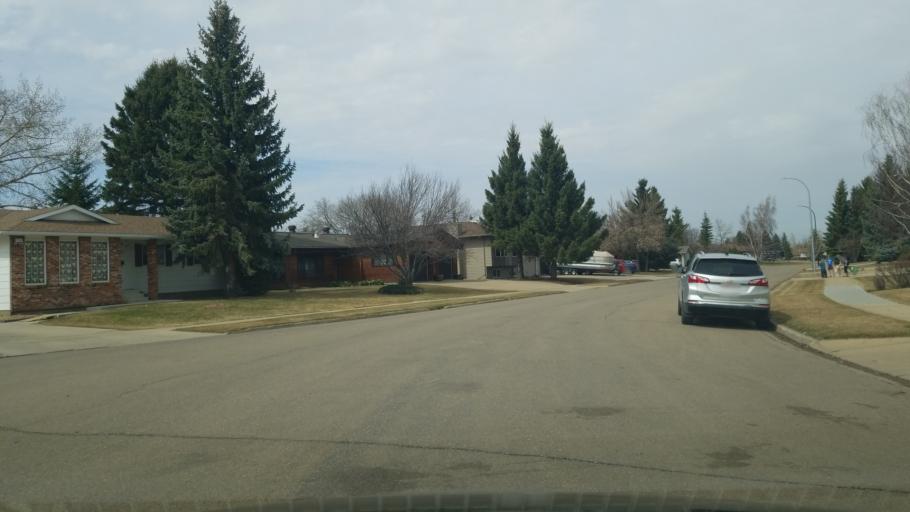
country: CA
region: Saskatchewan
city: Lloydminster
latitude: 53.2668
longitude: -110.0284
